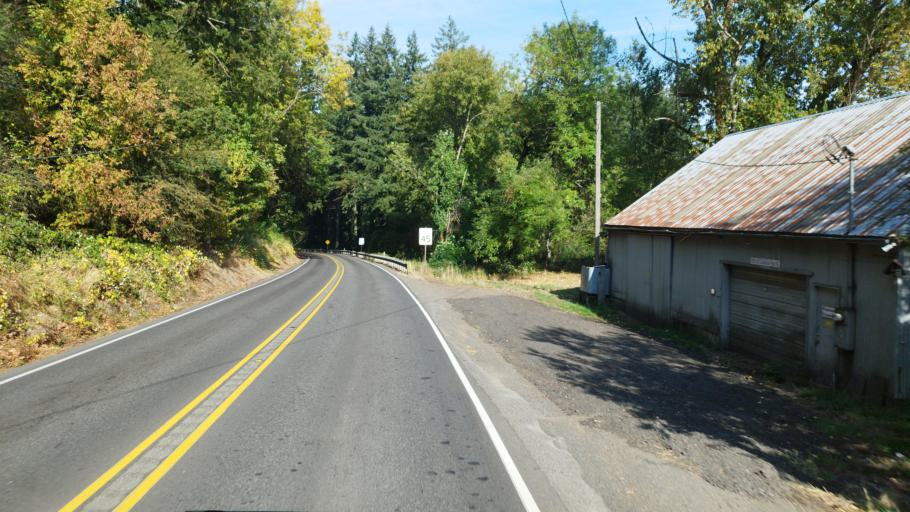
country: US
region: Oregon
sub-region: Washington County
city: Bethany
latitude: 45.6095
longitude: -122.8622
